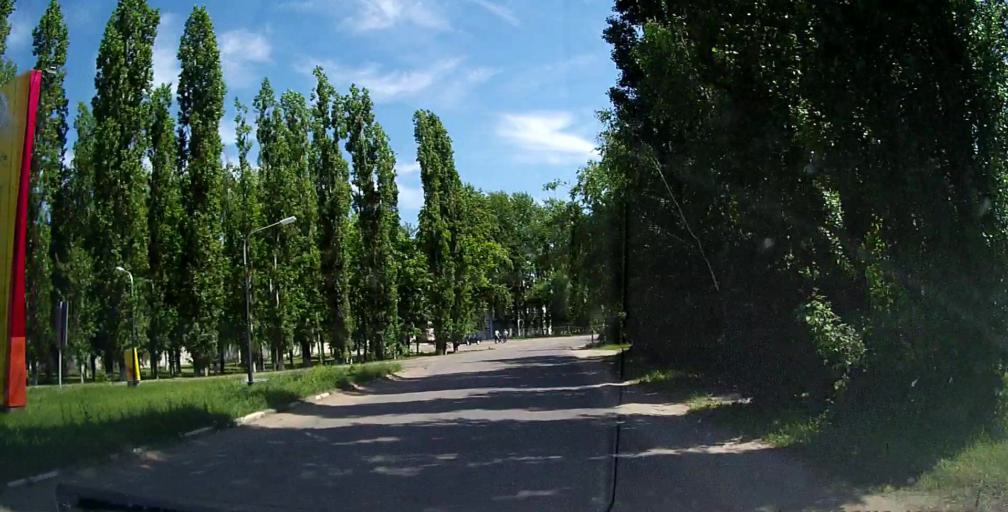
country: RU
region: Lipetsk
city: Chaplygin
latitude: 53.2487
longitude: 39.9743
